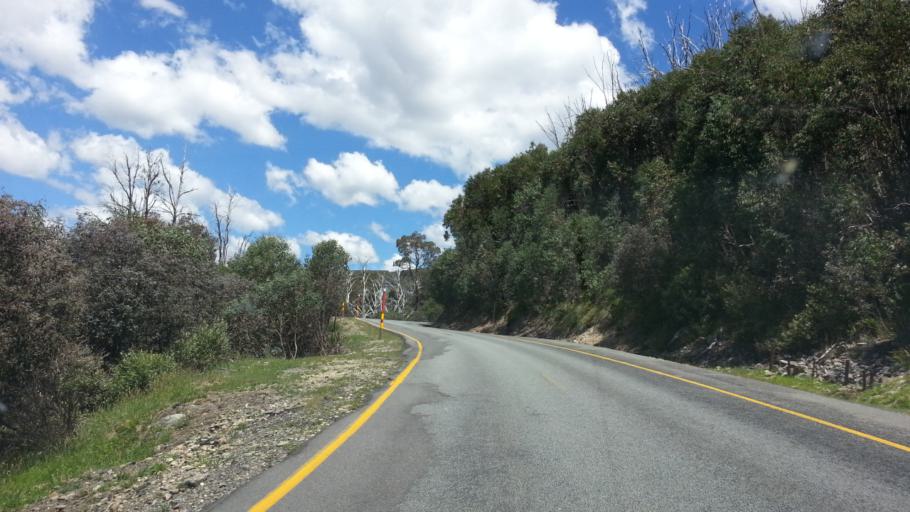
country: AU
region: Victoria
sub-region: Alpine
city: Mount Beauty
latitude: -36.8518
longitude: 147.2715
